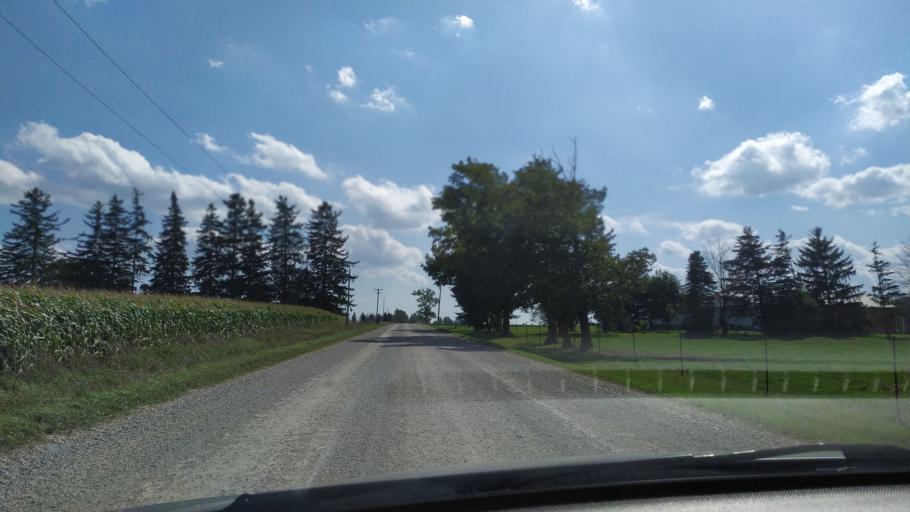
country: CA
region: Ontario
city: Stratford
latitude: 43.2727
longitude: -80.9226
